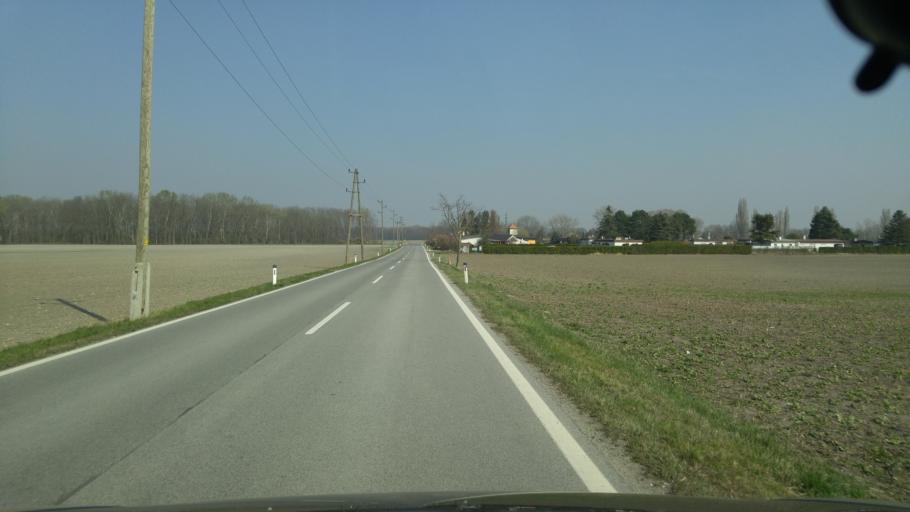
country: AT
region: Lower Austria
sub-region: Politischer Bezirk Wien-Umgebung
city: Moosbrunn
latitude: 48.0340
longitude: 16.4198
